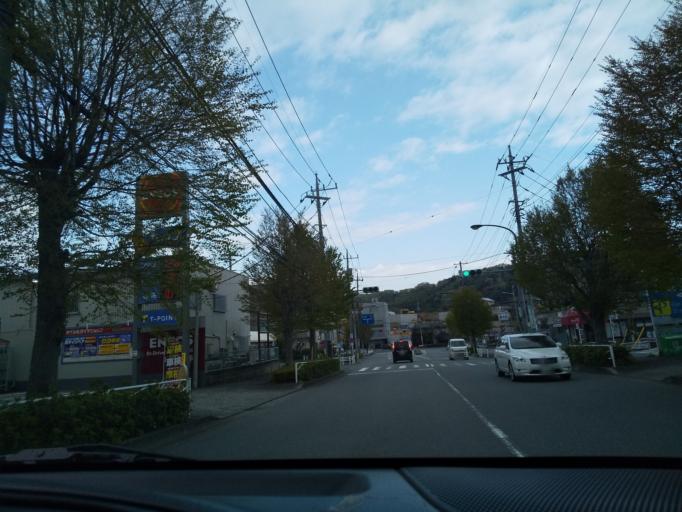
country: JP
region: Tokyo
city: Hino
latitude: 35.6227
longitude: 139.3765
